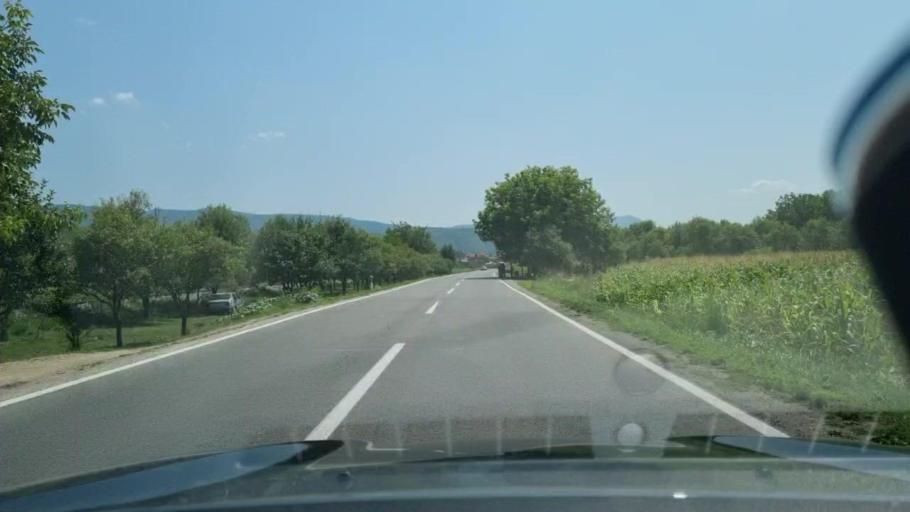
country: BA
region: Federation of Bosnia and Herzegovina
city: Bihac
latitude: 44.8050
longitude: 15.8988
